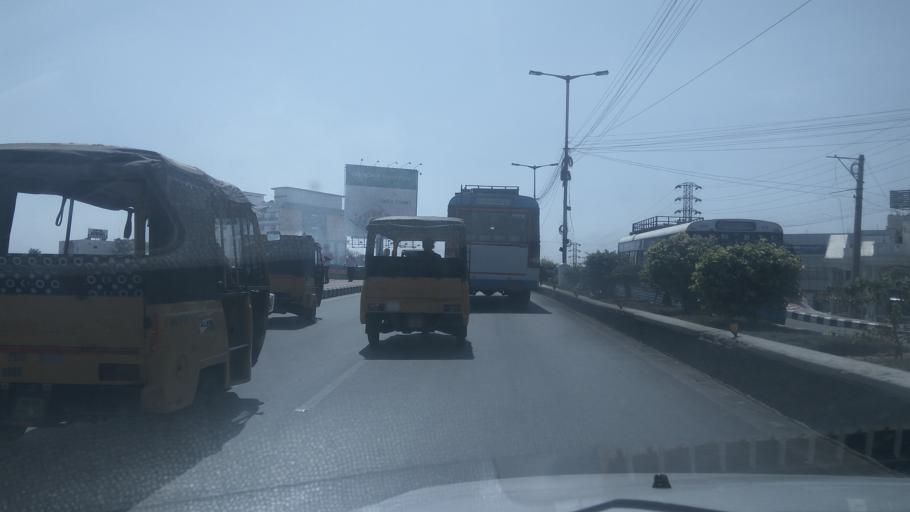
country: IN
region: Andhra Pradesh
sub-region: Chittoor
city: Tirupati
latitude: 13.6286
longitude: 79.4291
